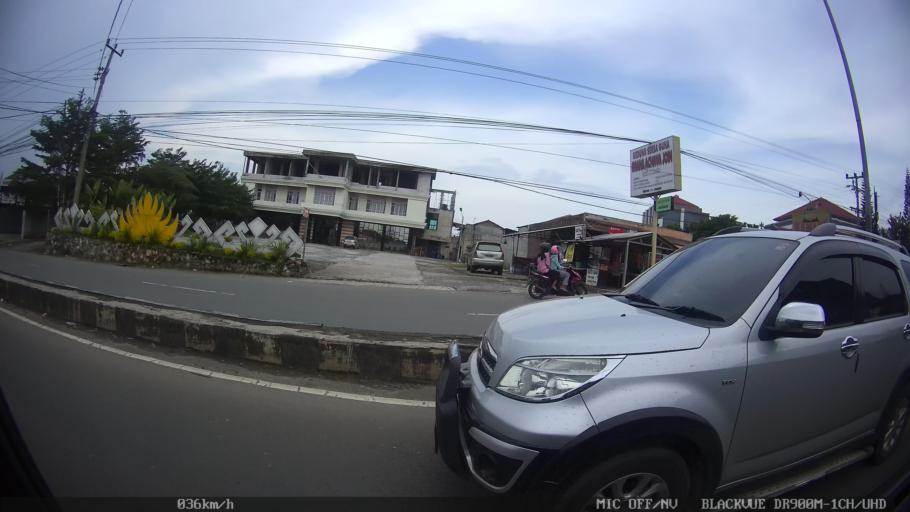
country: ID
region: Lampung
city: Kedaton
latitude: -5.3766
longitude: 105.2221
